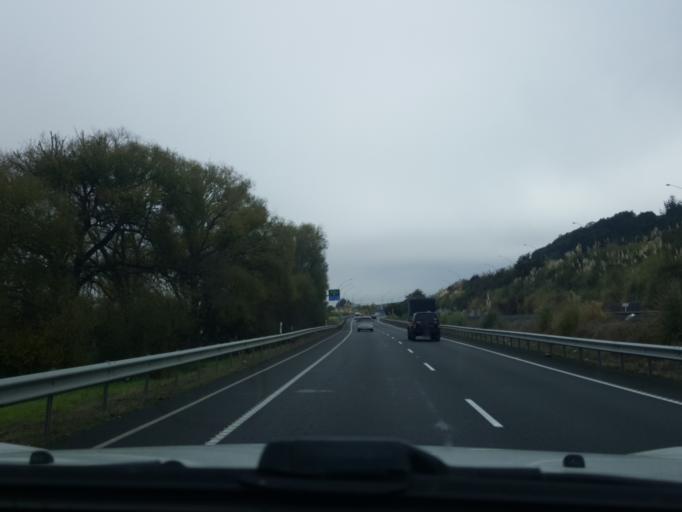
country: NZ
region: Auckland
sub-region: Auckland
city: Pukekohe East
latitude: -37.2834
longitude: 175.0505
